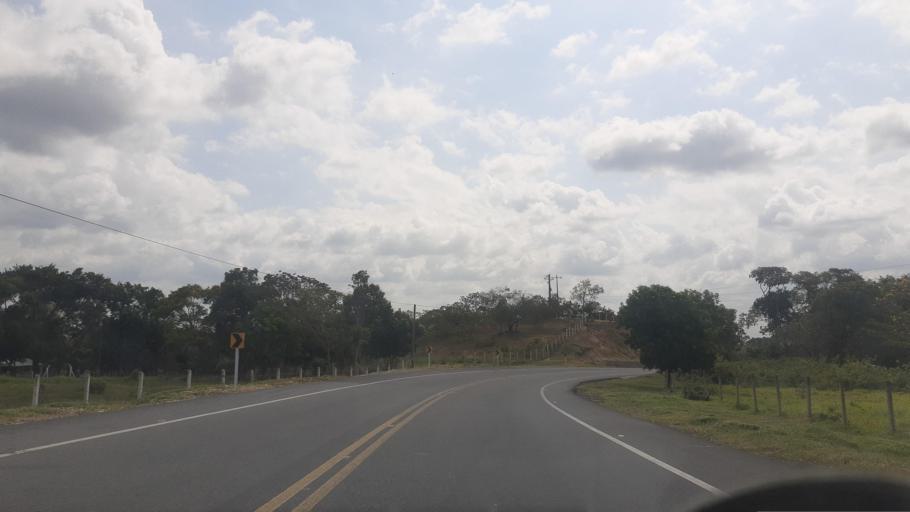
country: CO
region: Casanare
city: Monterrey
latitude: 4.8424
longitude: -72.8384
